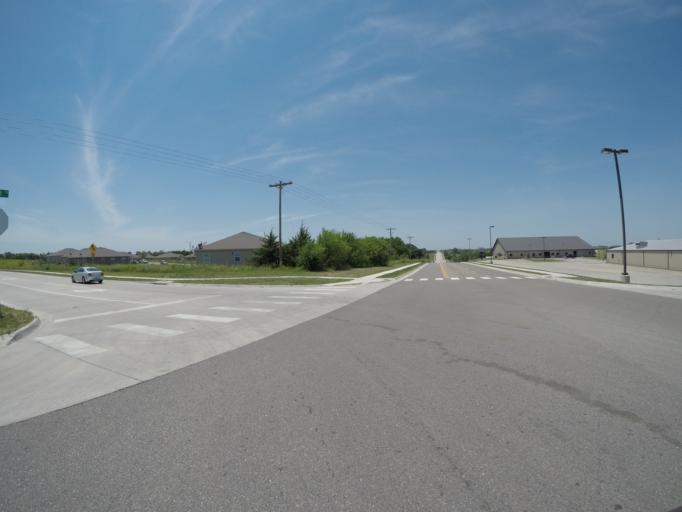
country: US
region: Kansas
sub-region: Geary County
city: Junction City
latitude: 39.0445
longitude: -96.8709
